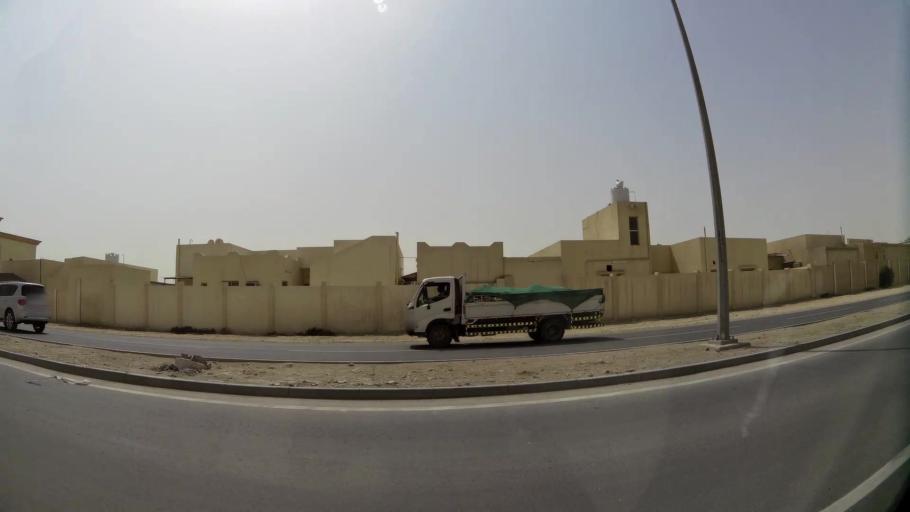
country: QA
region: Baladiyat ar Rayyan
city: Ar Rayyan
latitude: 25.2357
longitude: 51.3826
